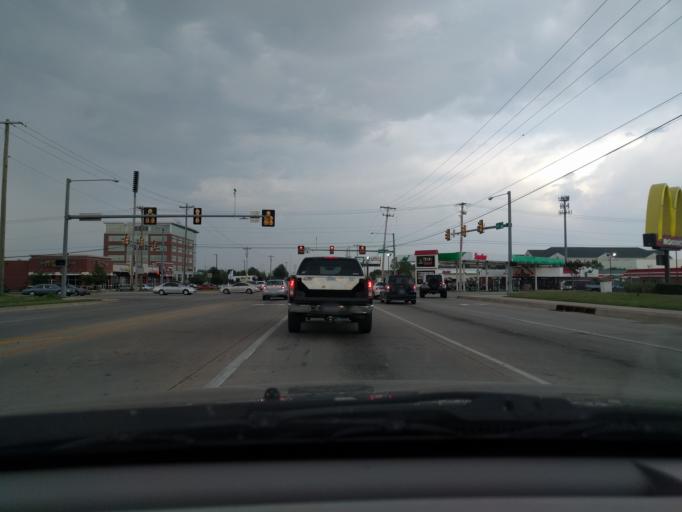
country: US
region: Oklahoma
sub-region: Tulsa County
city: Broken Arrow
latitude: 36.0463
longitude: -95.8694
